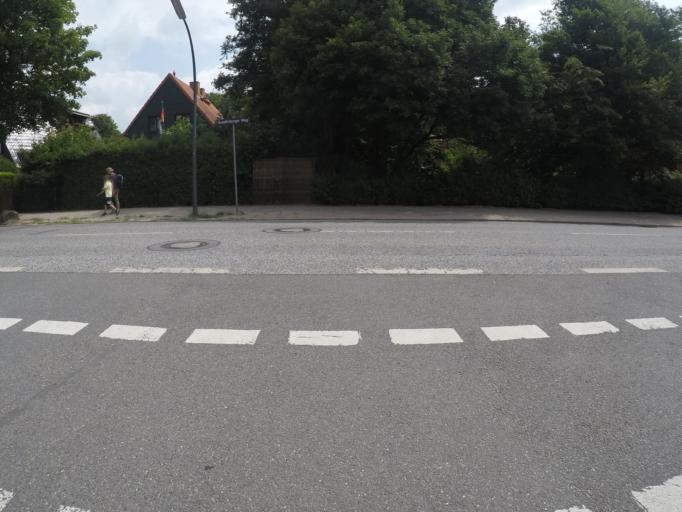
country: DE
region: Schleswig-Holstein
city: Bonningstedt
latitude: 53.6371
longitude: 9.9443
